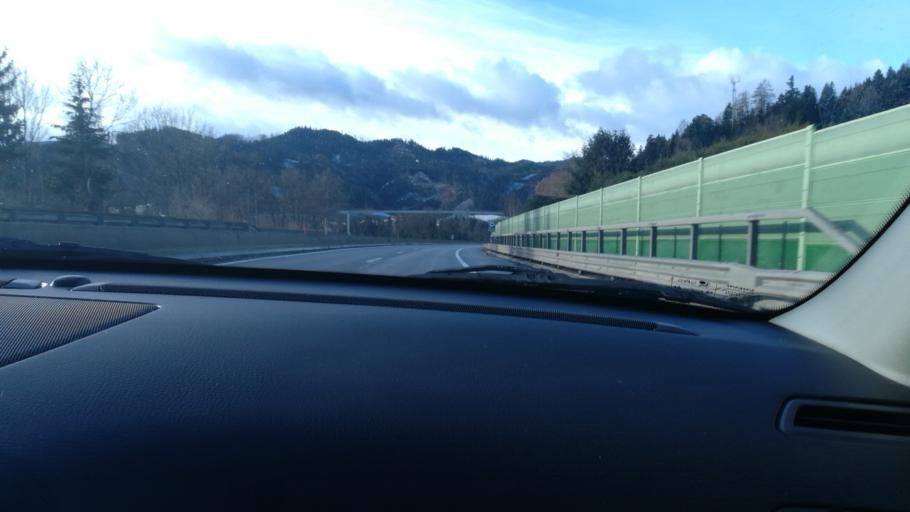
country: AT
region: Styria
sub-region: Politischer Bezirk Murtal
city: Judenburg
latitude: 47.1767
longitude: 14.6576
